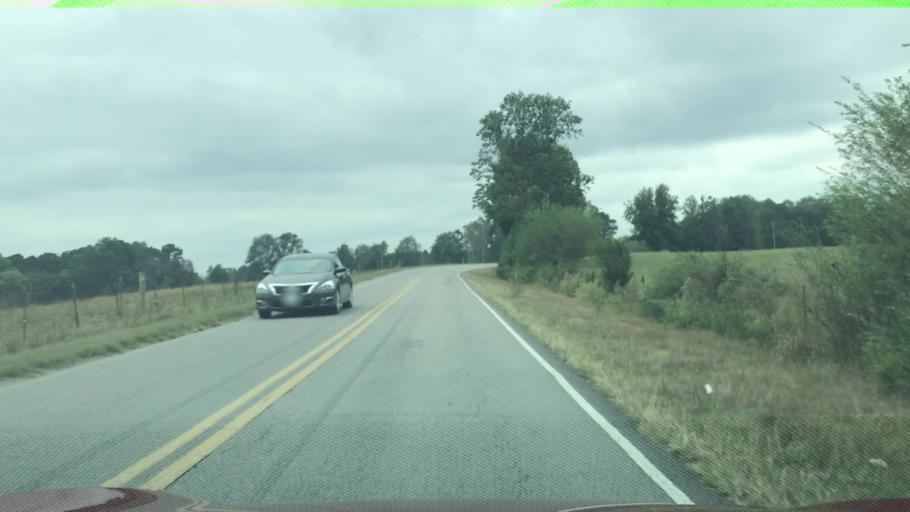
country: US
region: Alabama
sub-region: Cullman County
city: Good Hope
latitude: 34.0965
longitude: -87.0428
